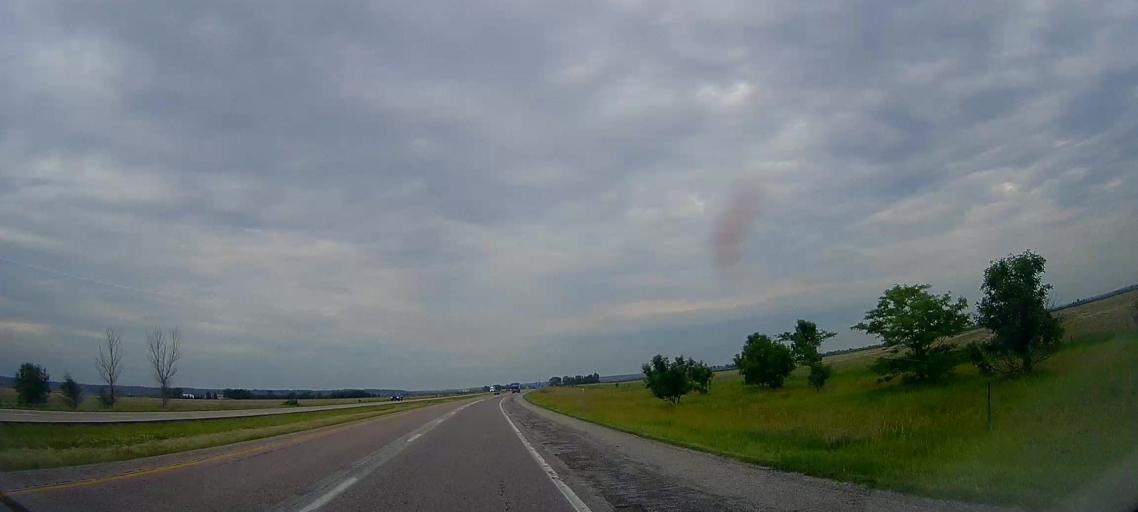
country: US
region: Iowa
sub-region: Harrison County
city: Missouri Valley
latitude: 41.6026
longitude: -95.9652
